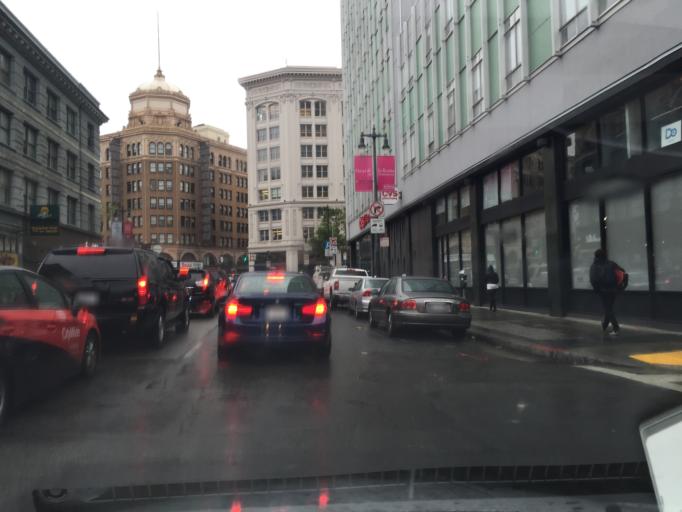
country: US
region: California
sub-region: San Francisco County
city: San Francisco
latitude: 37.7818
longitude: -122.4096
